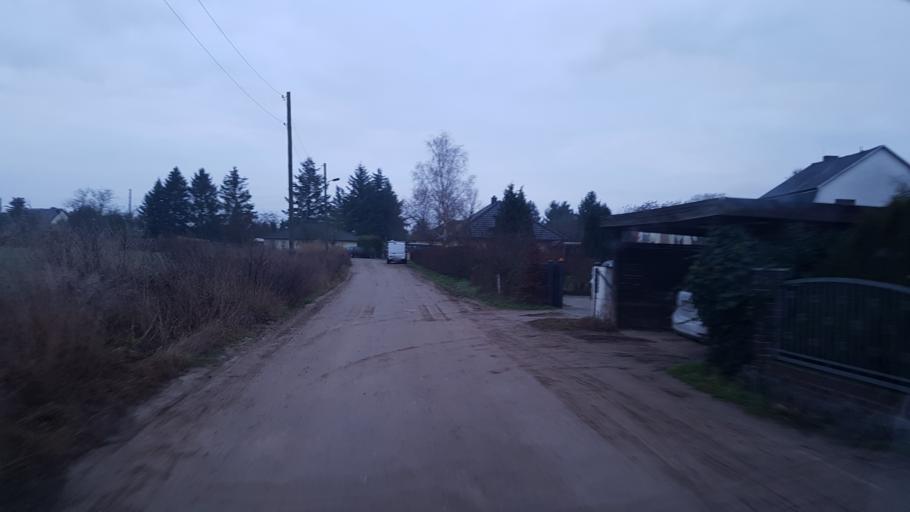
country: DE
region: Brandenburg
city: Stahnsdorf
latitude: 52.3645
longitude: 13.1972
